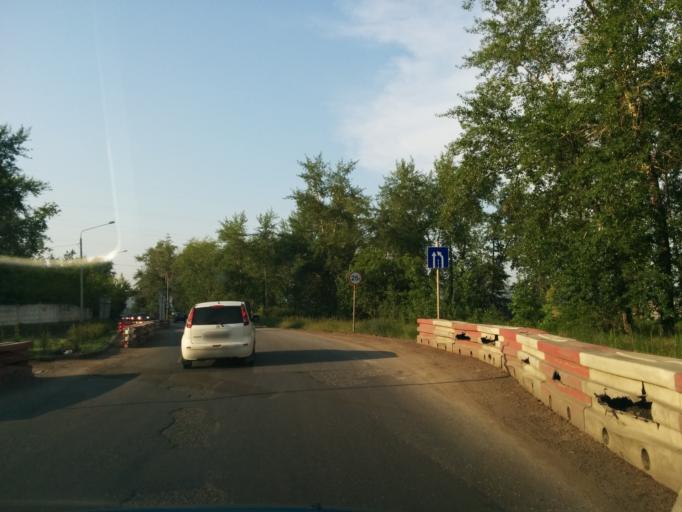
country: RU
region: Perm
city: Perm
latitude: 58.1108
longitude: 56.3236
